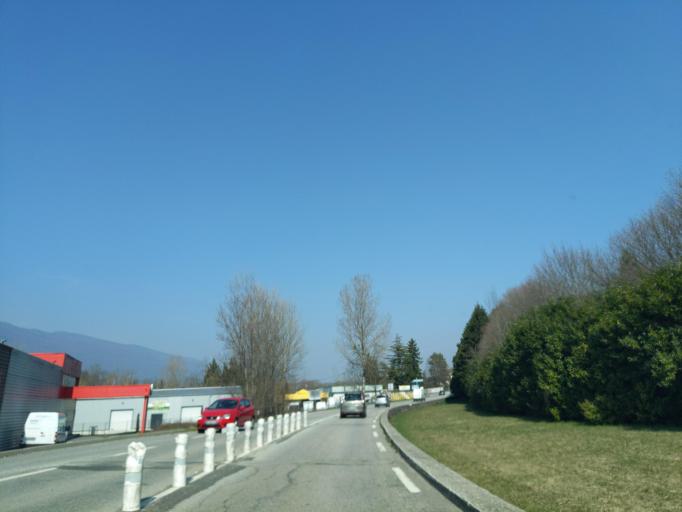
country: FR
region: Rhone-Alpes
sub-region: Departement de la Savoie
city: Chindrieux
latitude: 45.8467
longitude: 5.8373
